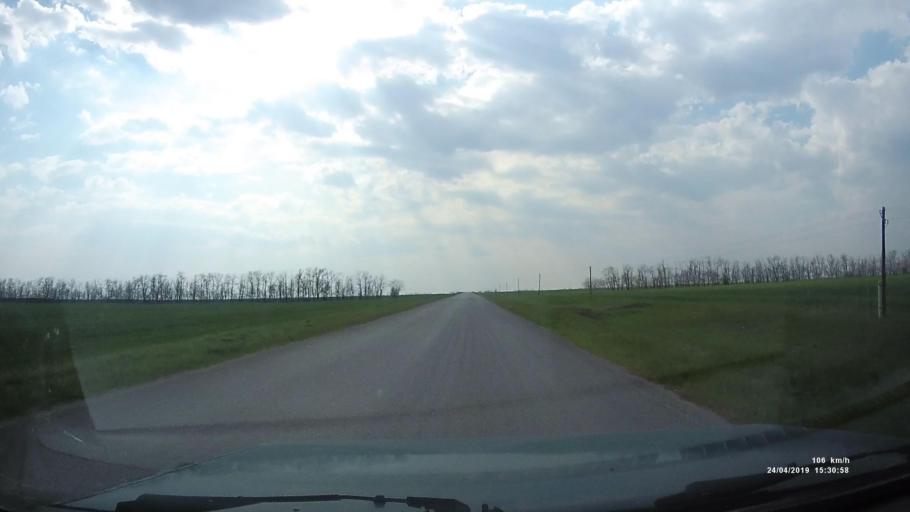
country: RU
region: Rostov
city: Remontnoye
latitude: 46.5998
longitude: 42.9953
